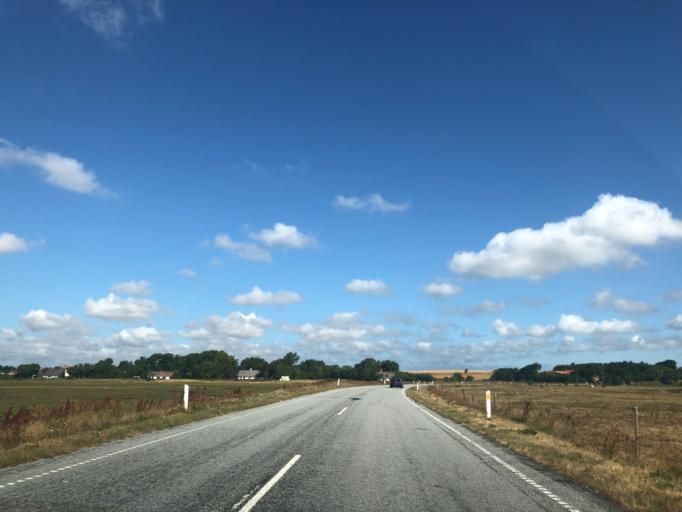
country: DK
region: North Denmark
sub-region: Morso Kommune
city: Nykobing Mors
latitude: 56.9822
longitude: 8.9112
